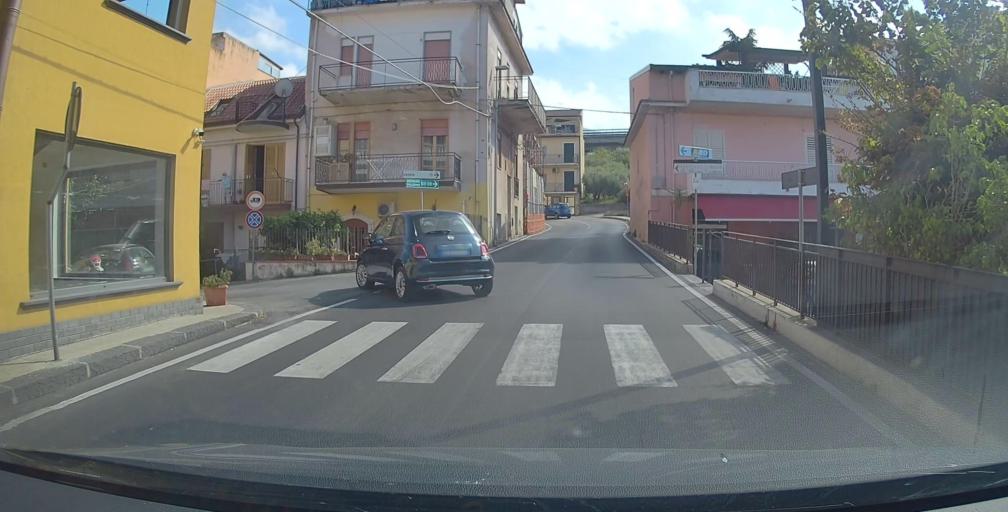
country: IT
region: Sicily
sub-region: Messina
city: Patti
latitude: 38.1525
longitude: 14.9675
